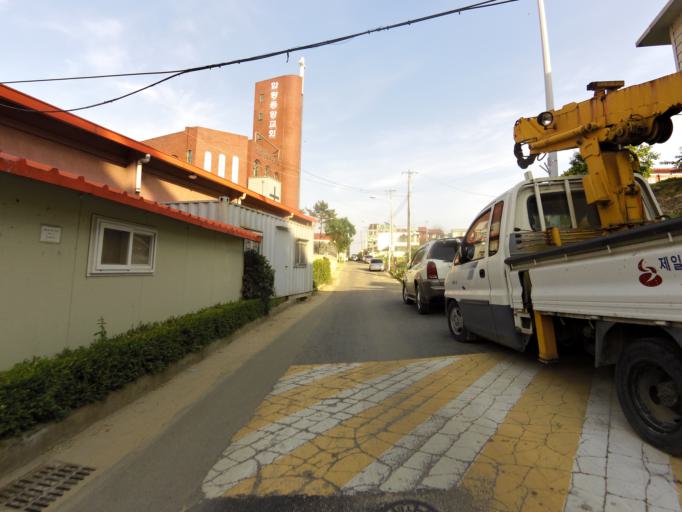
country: KR
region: Gyeongsangbuk-do
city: Gyeongsan-si
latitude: 35.8401
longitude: 128.7598
